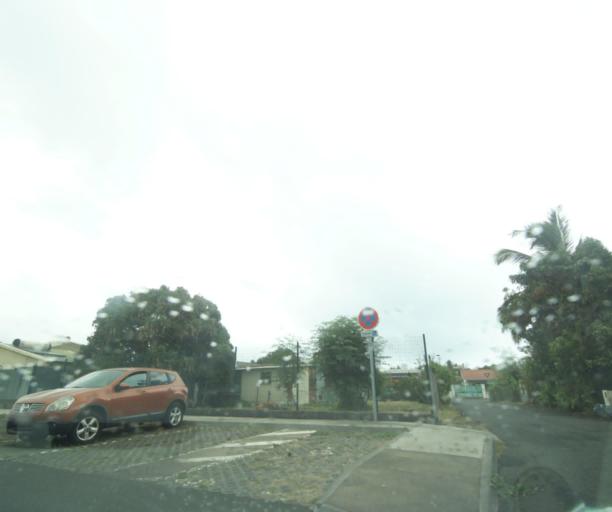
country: RE
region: Reunion
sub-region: Reunion
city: Saint-Paul
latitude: -20.9931
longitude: 55.2857
